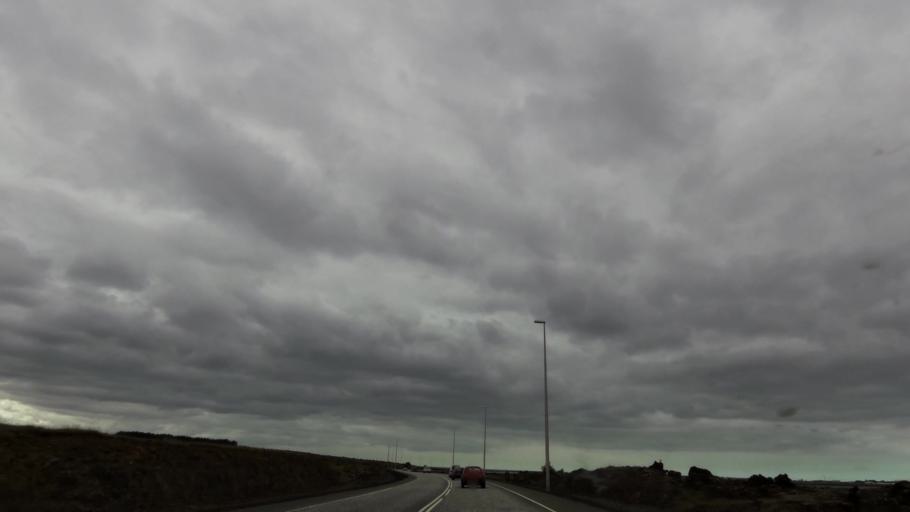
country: IS
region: Capital Region
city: Hafnarfjoerdur
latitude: 64.0905
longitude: -21.9716
